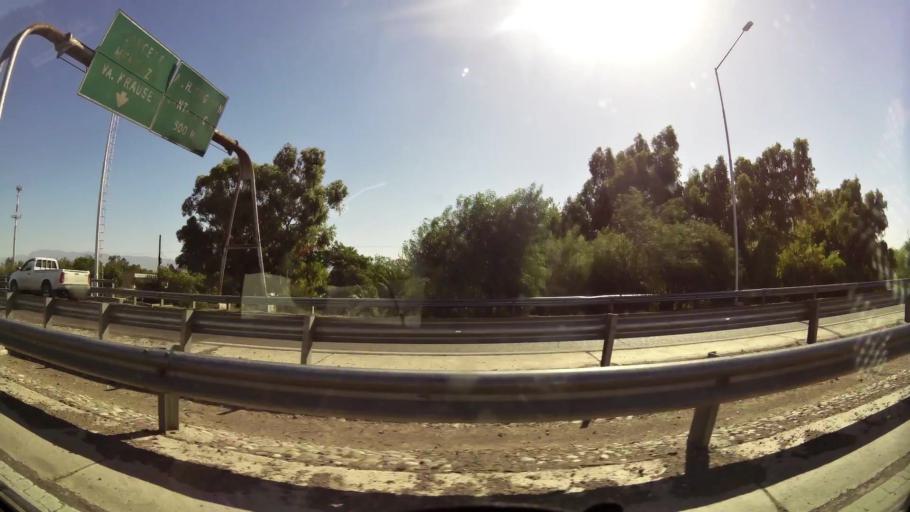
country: AR
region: San Juan
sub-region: Departamento de Santa Lucia
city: Santa Lucia
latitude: -31.5328
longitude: -68.5039
